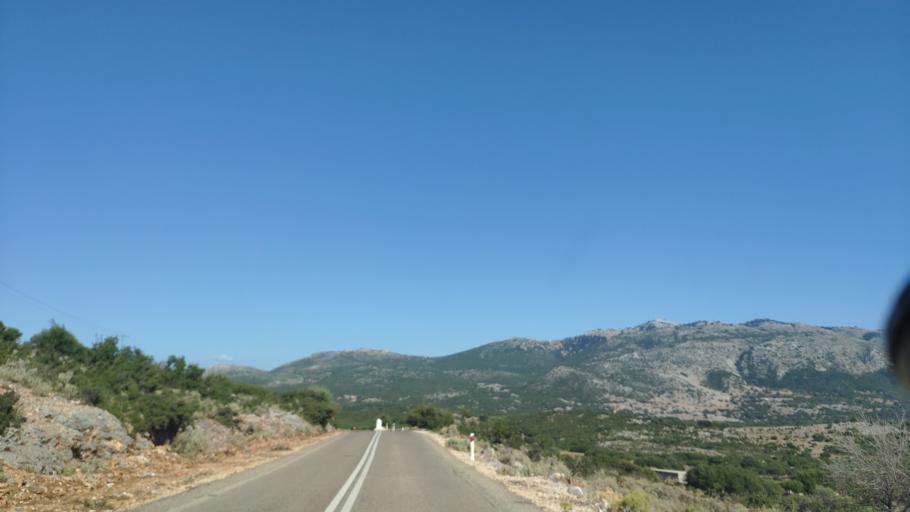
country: GR
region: West Greece
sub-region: Nomos Aitolias kai Akarnanias
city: Archontochorion
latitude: 38.6919
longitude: 21.0405
